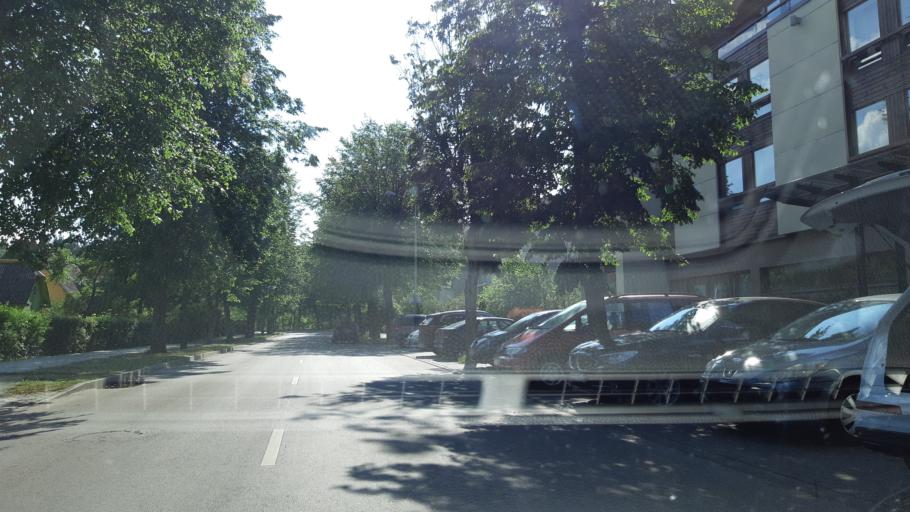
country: LT
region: Alytaus apskritis
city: Druskininkai
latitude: 54.0108
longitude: 23.9841
